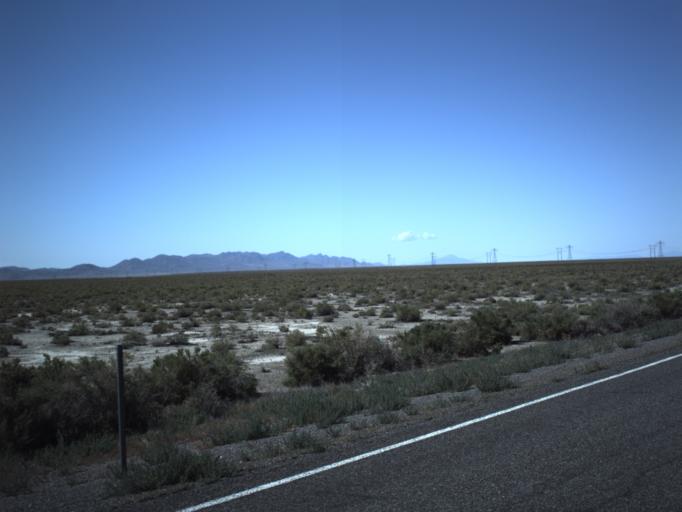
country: US
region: Utah
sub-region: Millard County
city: Delta
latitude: 39.2531
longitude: -112.8928
